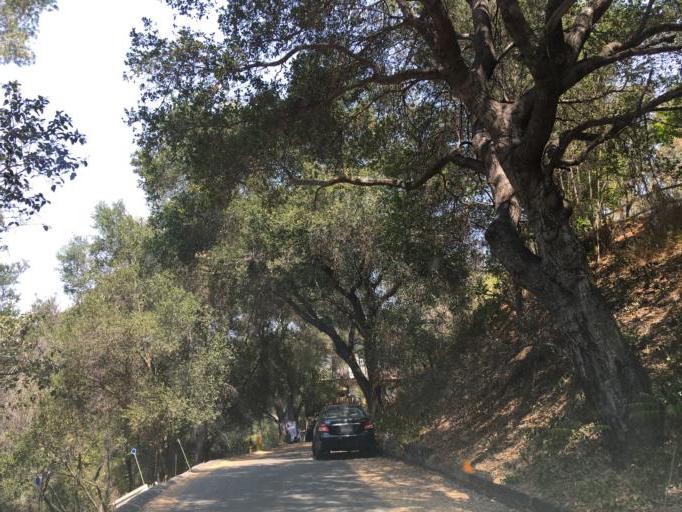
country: US
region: California
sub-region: Los Angeles County
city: Topanga
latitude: 34.1050
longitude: -118.5913
